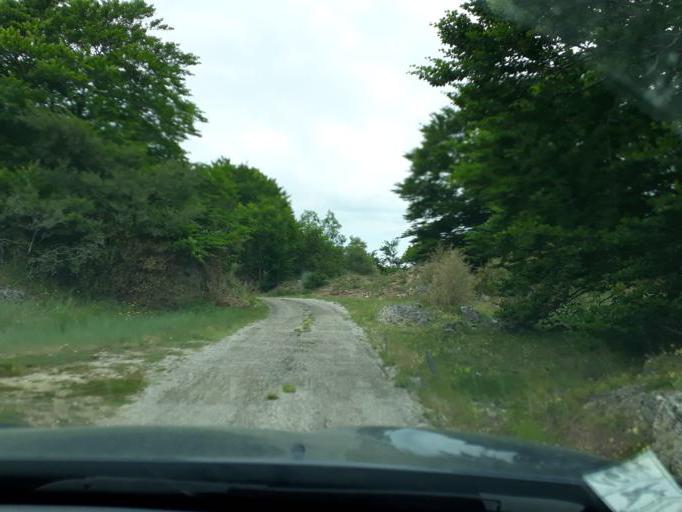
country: FR
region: Languedoc-Roussillon
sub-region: Departement de l'Herault
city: Lodeve
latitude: 43.8111
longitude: 3.2676
